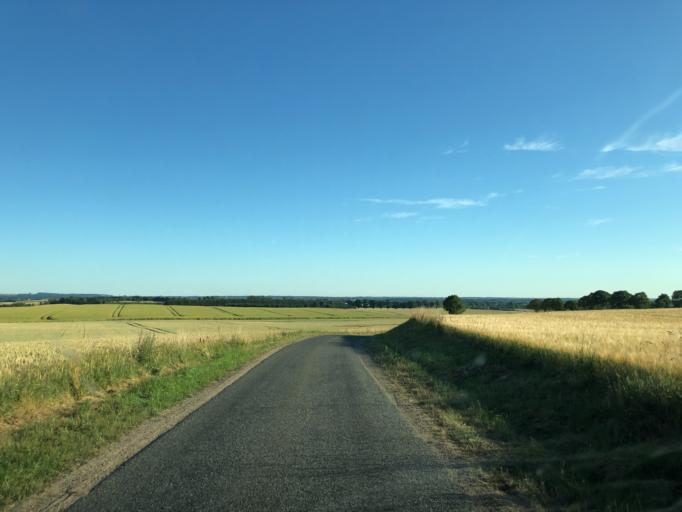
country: DK
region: Central Jutland
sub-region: Horsens Kommune
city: Horsens
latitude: 55.9086
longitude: 9.8728
